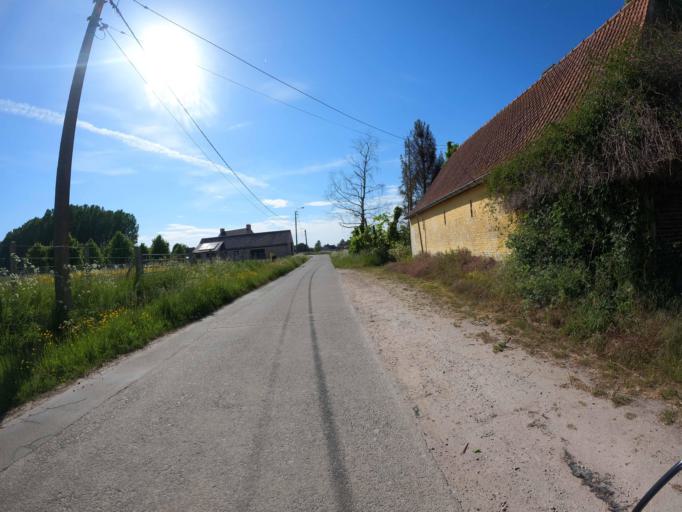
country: BE
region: Flanders
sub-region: Provincie Oost-Vlaanderen
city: Oosterzele
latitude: 50.9262
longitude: 3.7618
